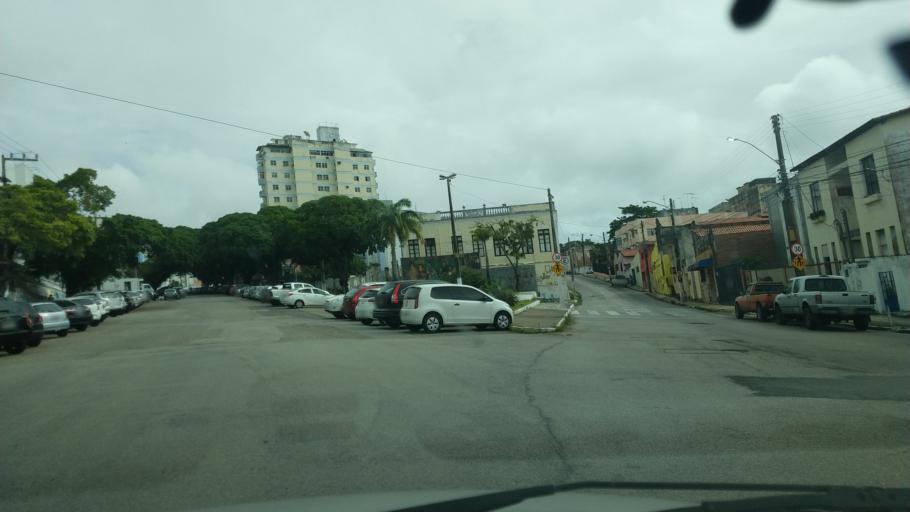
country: BR
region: Rio Grande do Norte
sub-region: Natal
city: Natal
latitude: -5.7825
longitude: -35.2070
